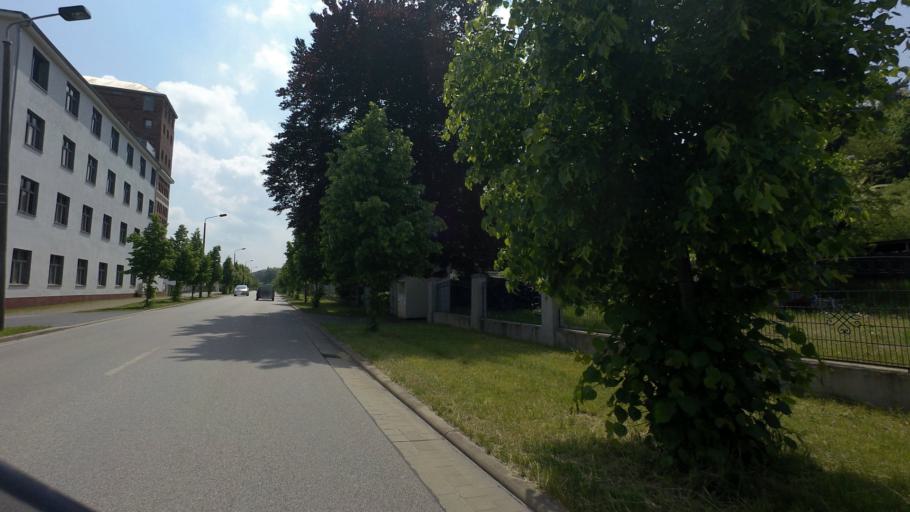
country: DE
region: Brandenburg
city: Spremberg
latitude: 51.5781
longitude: 14.3626
